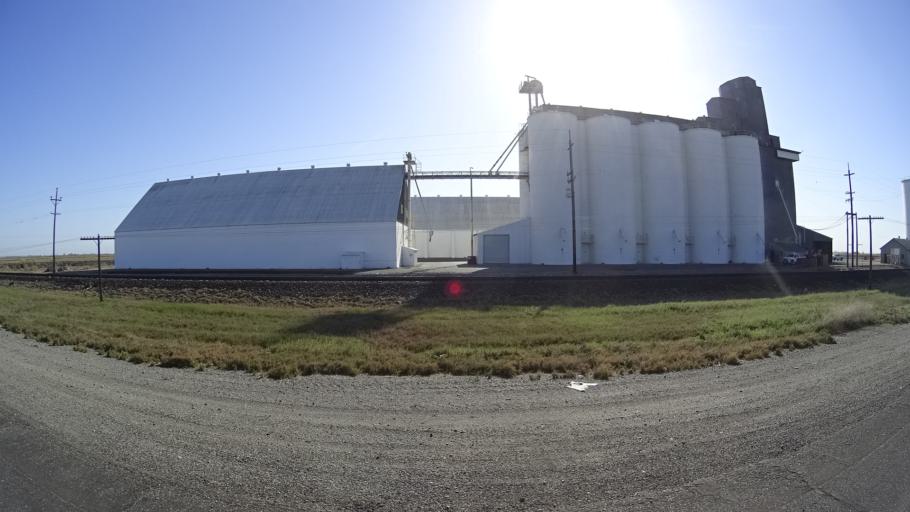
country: US
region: California
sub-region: Glenn County
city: Willows
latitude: 39.4668
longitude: -122.1931
